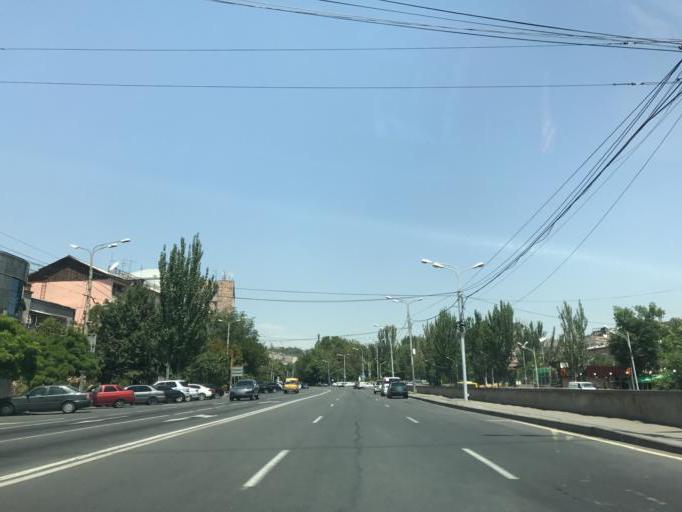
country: AM
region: Yerevan
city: Yerevan
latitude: 40.1800
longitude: 44.5236
